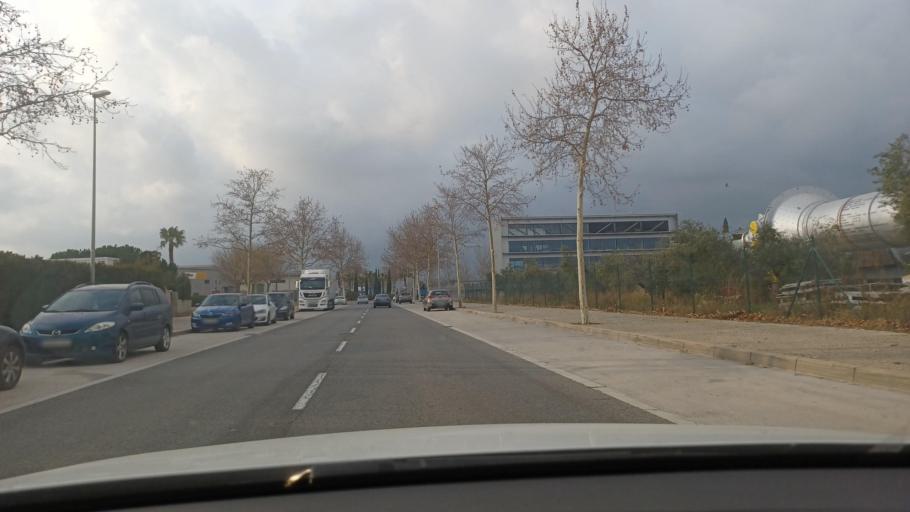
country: ES
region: Catalonia
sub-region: Provincia de Tarragona
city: Vila-seca
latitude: 41.1158
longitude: 1.1536
